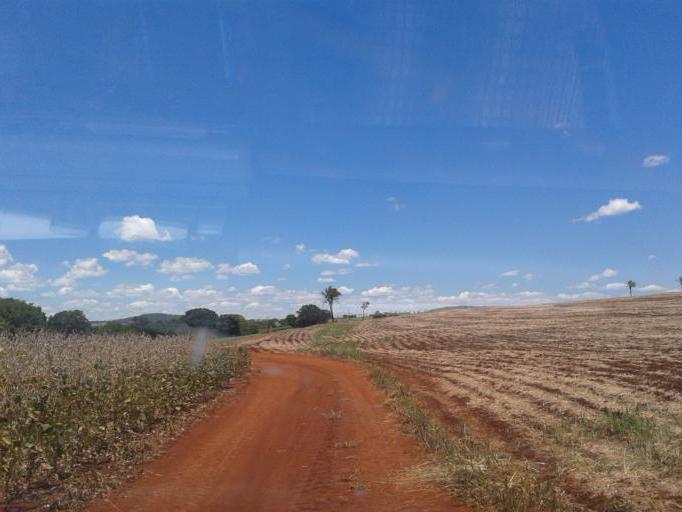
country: BR
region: Minas Gerais
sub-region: Capinopolis
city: Capinopolis
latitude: -18.5649
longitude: -49.5402
